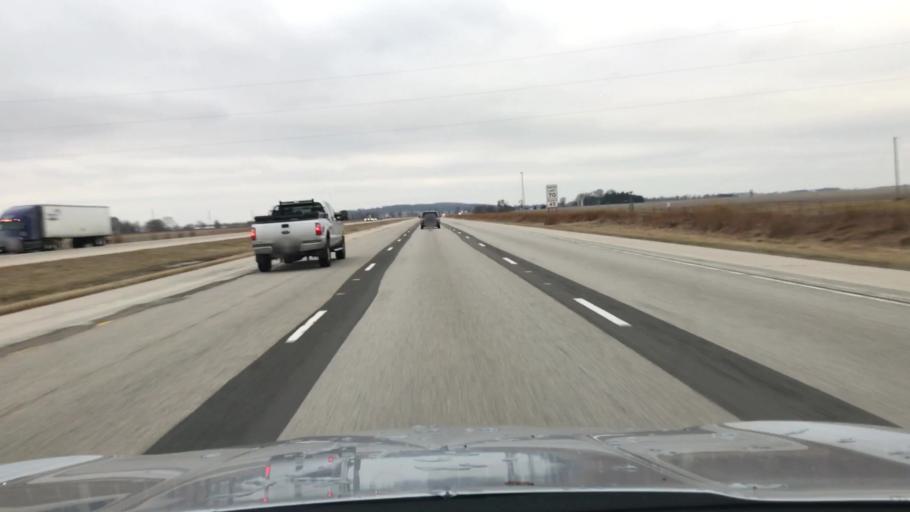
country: US
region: Illinois
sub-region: Logan County
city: Lincoln
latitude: 40.0678
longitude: -89.4471
